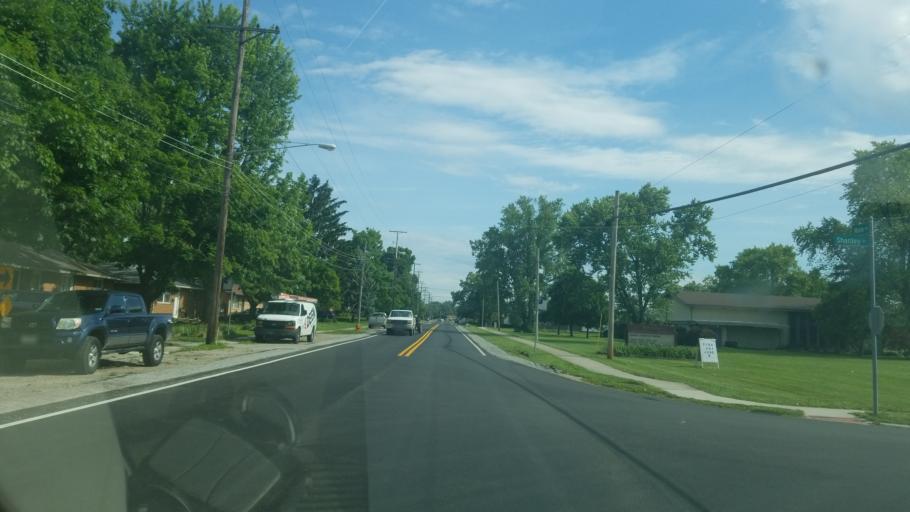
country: US
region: Ohio
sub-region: Franklin County
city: Worthington
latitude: 40.0563
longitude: -82.9877
